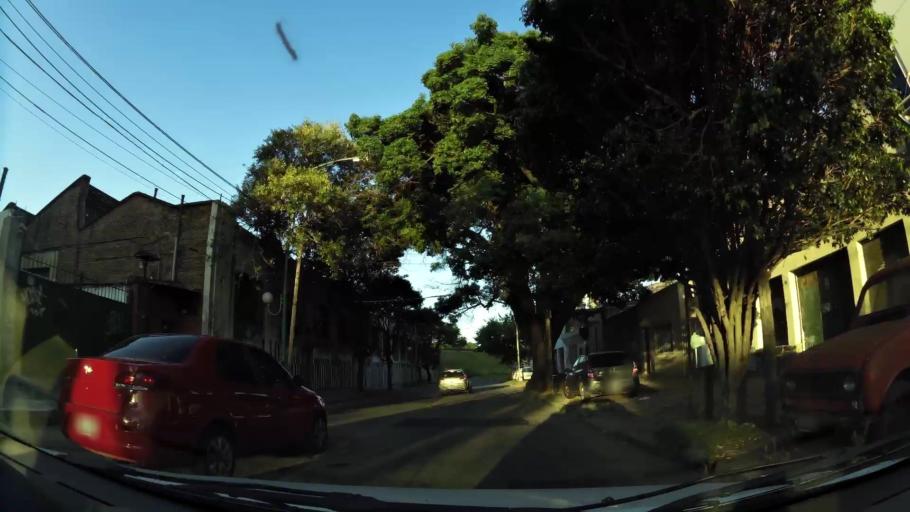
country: AR
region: Buenos Aires
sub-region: Partido de General San Martin
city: General San Martin
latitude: -34.5450
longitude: -58.4978
